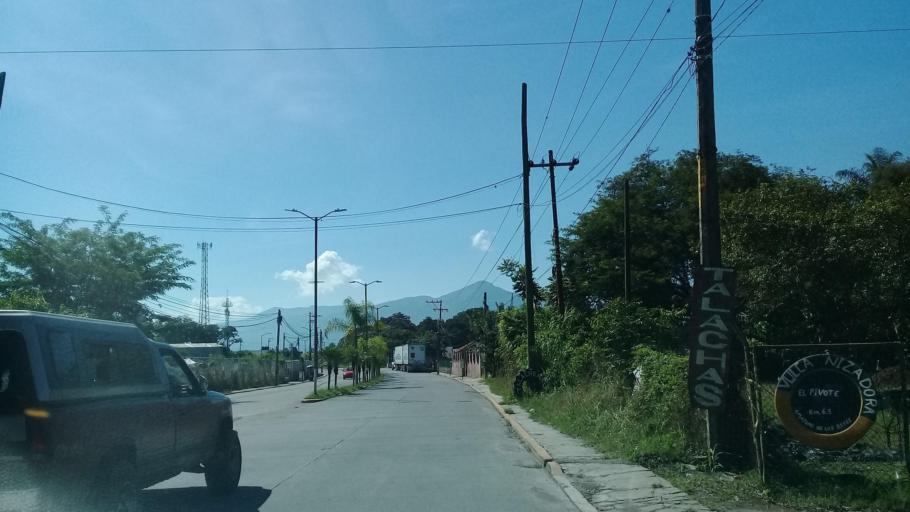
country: MX
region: Veracruz
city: Amatlan de los Reyes
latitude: 18.8564
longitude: -96.9127
